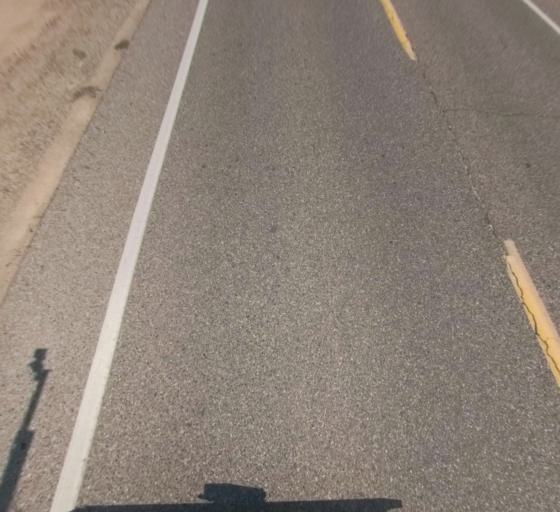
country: US
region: California
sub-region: Madera County
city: Fairmead
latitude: 37.0627
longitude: -120.1470
